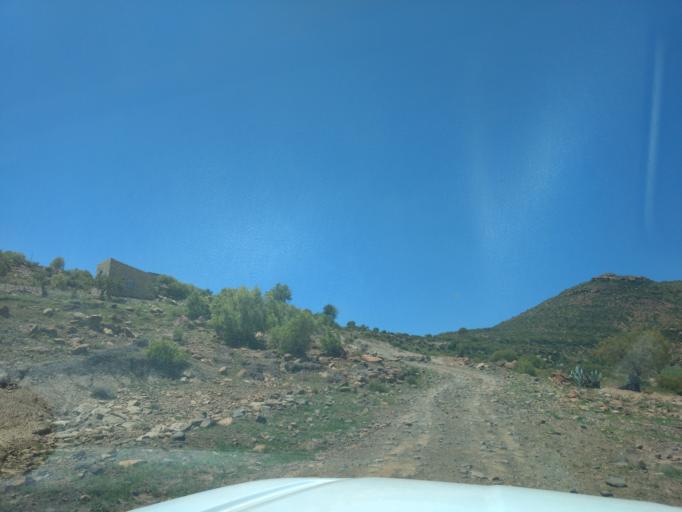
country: LS
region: Maseru
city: Maseru
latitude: -29.4598
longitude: 27.3740
